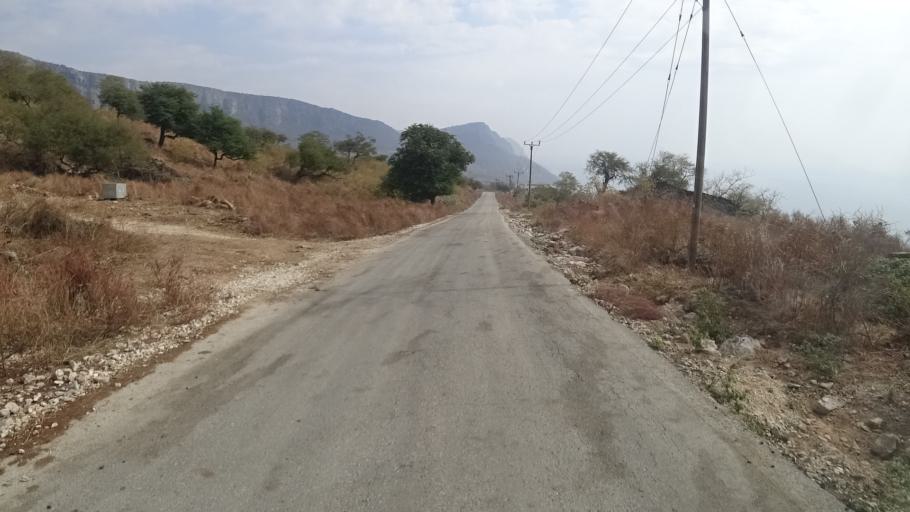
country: YE
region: Al Mahrah
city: Hawf
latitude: 16.7101
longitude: 53.2429
